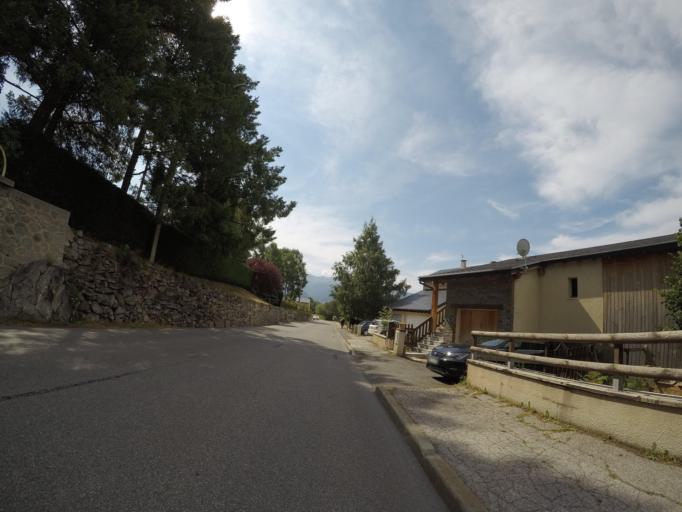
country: ES
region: Catalonia
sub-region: Provincia de Girona
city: Llivia
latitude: 42.4960
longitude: 2.0347
